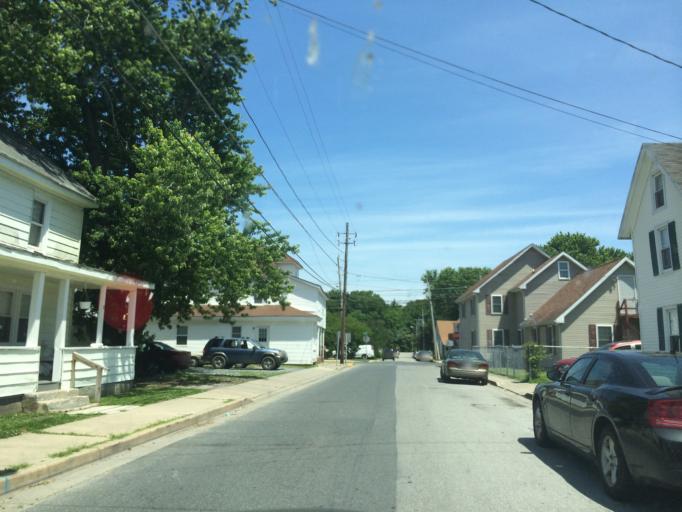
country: US
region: Maryland
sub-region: Wicomico County
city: Delmar
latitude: 38.4556
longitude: -75.5799
